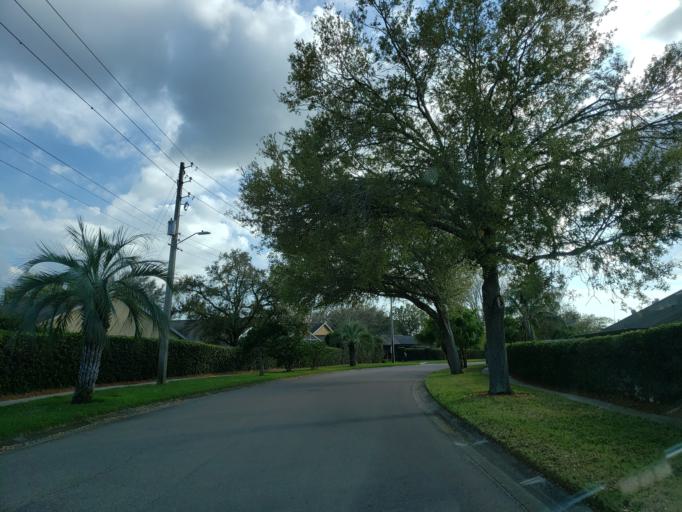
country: US
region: Florida
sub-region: Hillsborough County
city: Brandon
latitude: 27.9047
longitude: -82.3046
